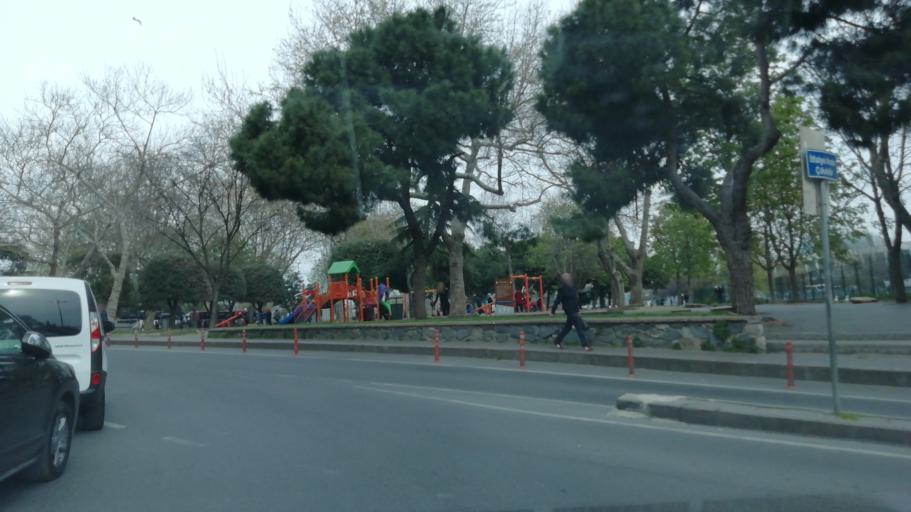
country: TR
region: Istanbul
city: Istanbul
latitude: 41.0146
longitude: 28.9522
